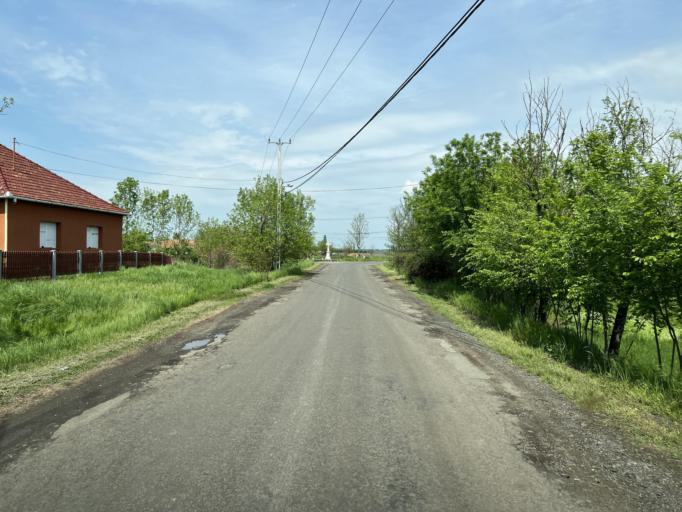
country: HU
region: Pest
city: Tapiogyorgye
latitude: 47.3440
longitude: 19.9447
